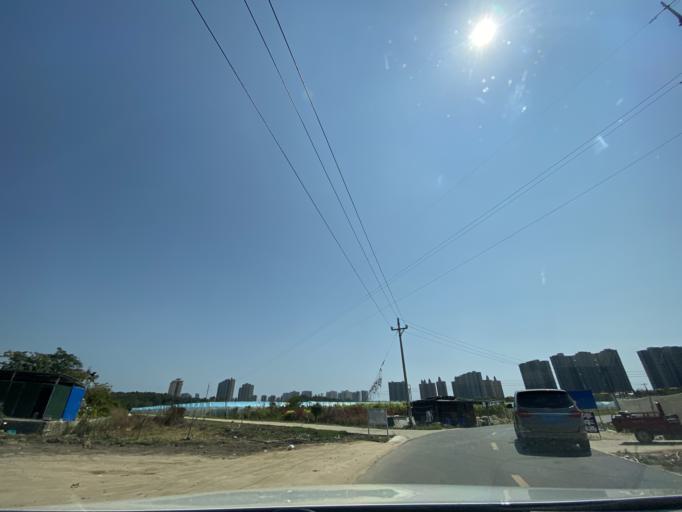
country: CN
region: Hainan
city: Yingzhou
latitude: 18.4201
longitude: 109.8786
